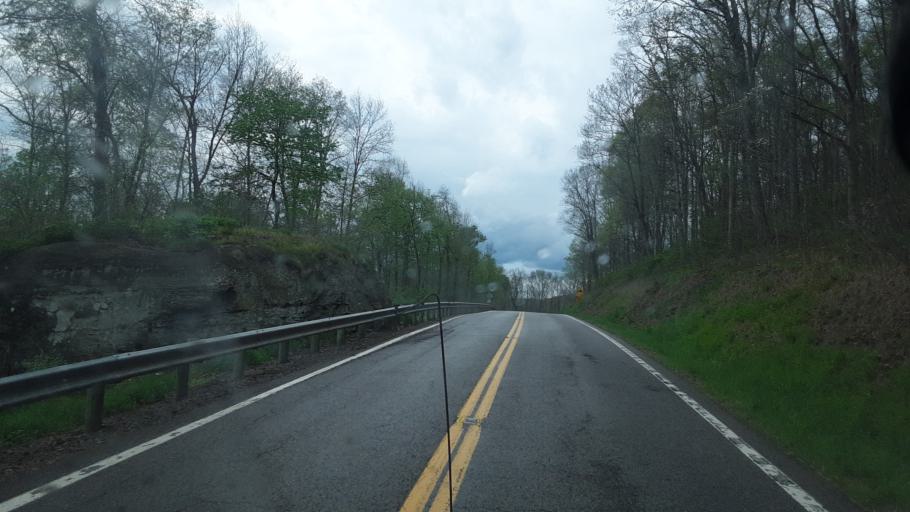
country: US
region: Ohio
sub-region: Guernsey County
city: Mantua
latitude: 40.0905
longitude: -81.7678
